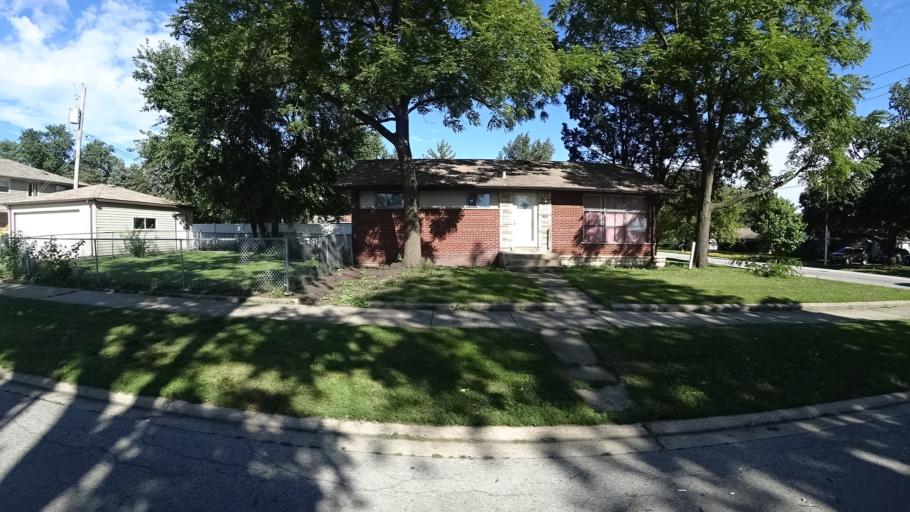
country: US
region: Illinois
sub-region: Cook County
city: Oak Lawn
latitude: 41.7128
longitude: -87.7502
